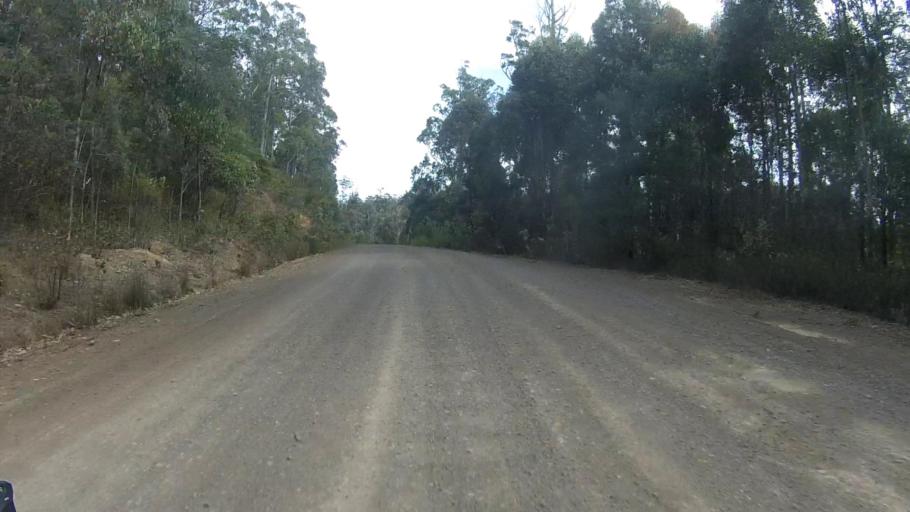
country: AU
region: Tasmania
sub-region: Sorell
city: Sorell
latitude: -42.7554
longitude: 147.8295
